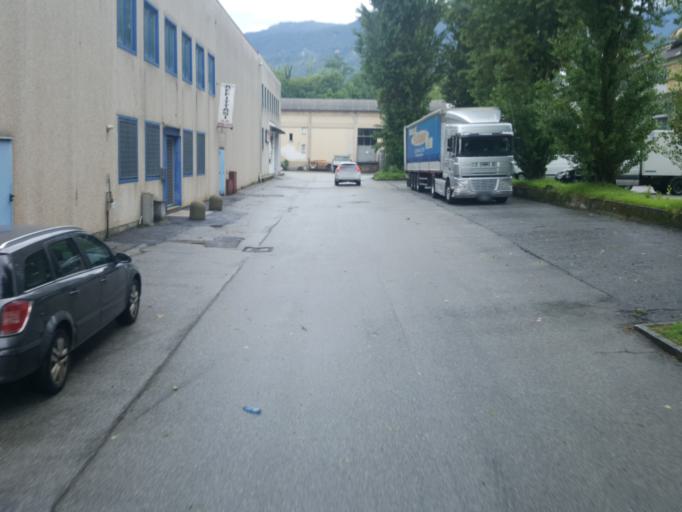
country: IT
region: Piedmont
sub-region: Provincia Verbano-Cusio-Ossola
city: Cambiasca
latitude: 45.9527
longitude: 8.5532
